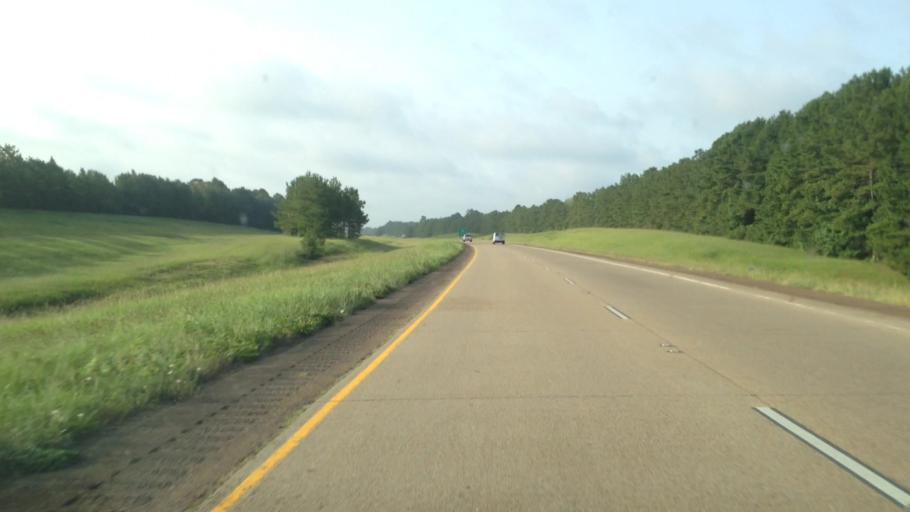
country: US
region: Louisiana
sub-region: Rapides Parish
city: Lecompte
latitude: 31.0920
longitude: -92.4446
